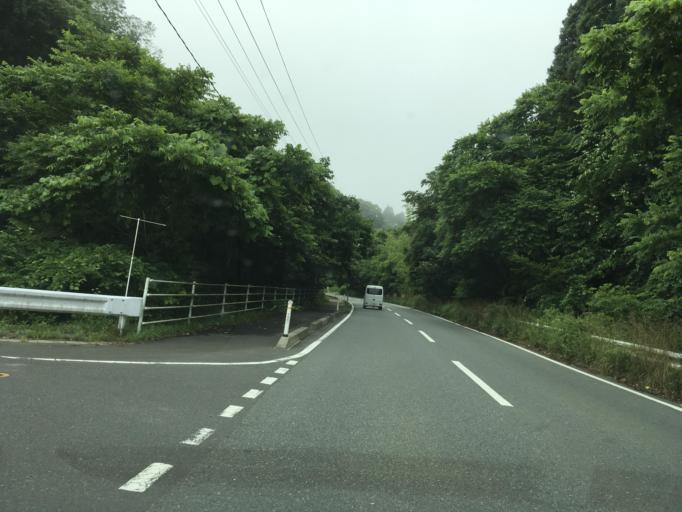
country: JP
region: Iwate
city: Ofunato
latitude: 38.9066
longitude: 141.6440
